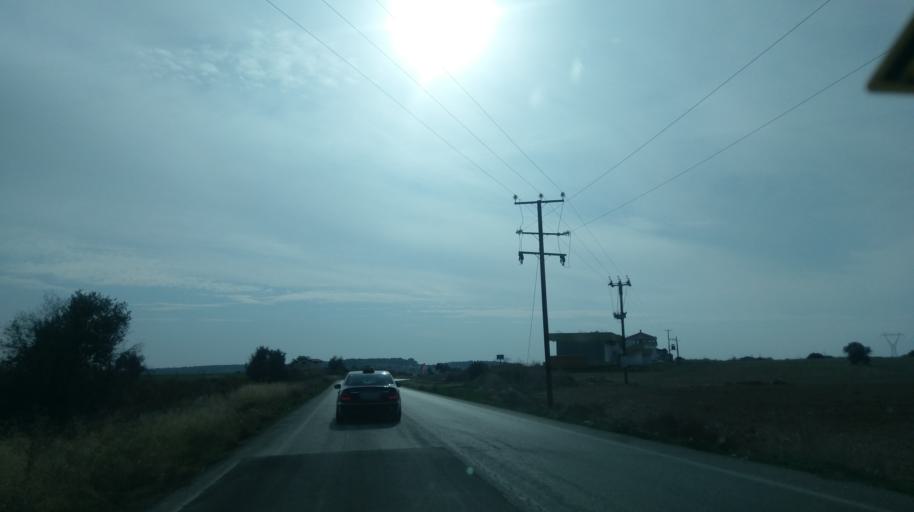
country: CY
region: Ammochostos
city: Leonarisso
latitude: 35.3782
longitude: 34.0381
